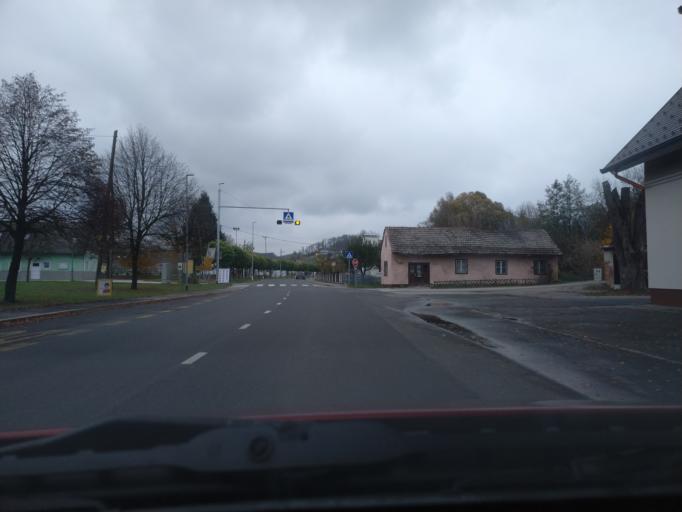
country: SI
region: Pesnica
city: Pesnica pri Mariboru
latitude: 46.6047
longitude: 15.6488
